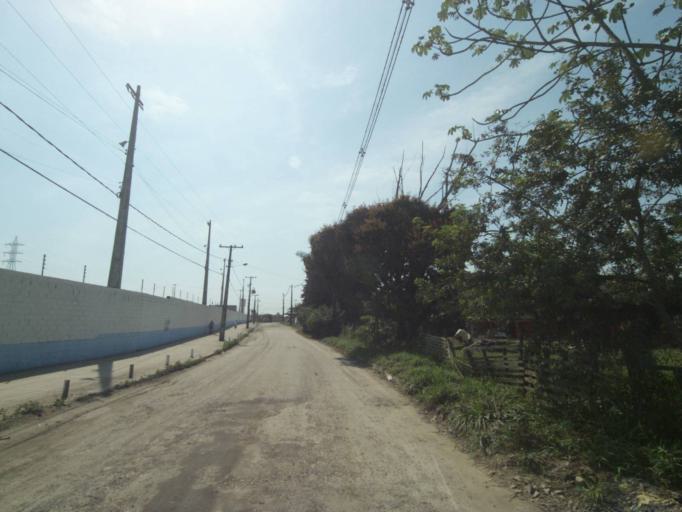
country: BR
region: Parana
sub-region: Paranagua
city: Paranagua
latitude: -25.5510
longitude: -48.5573
